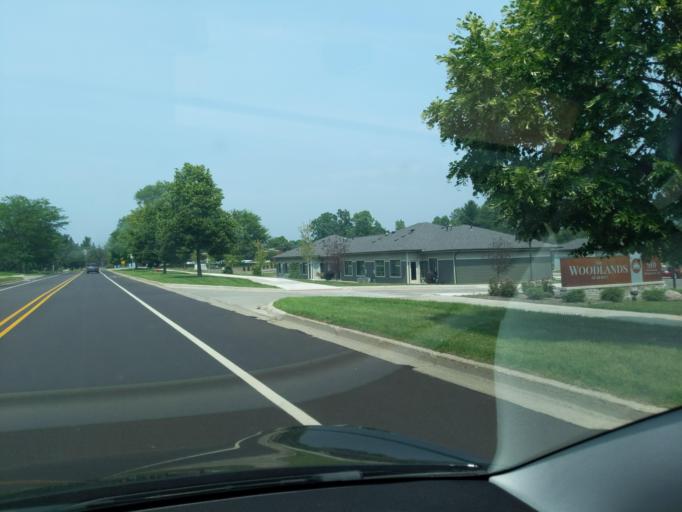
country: US
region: Michigan
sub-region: Clinton County
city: DeWitt
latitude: 42.8349
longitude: -84.5711
